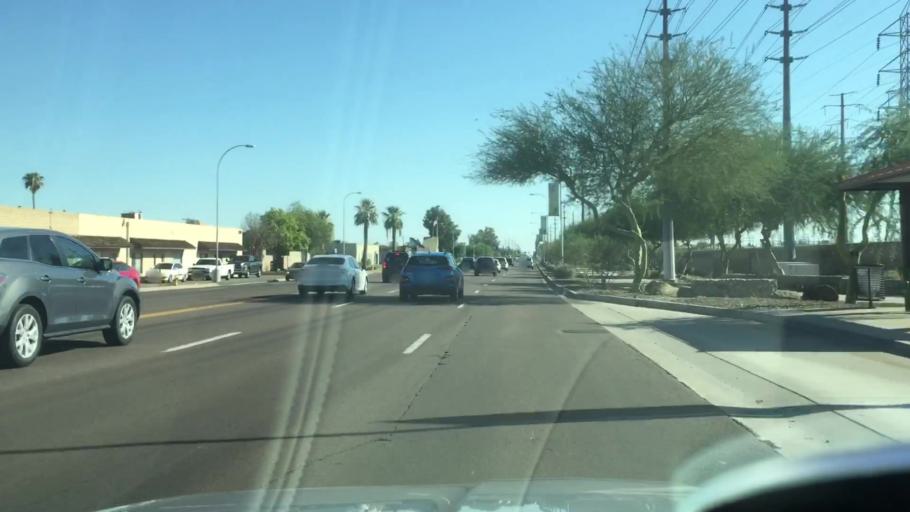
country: US
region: Arizona
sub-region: Maricopa County
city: Tempe
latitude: 33.4287
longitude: -111.9092
